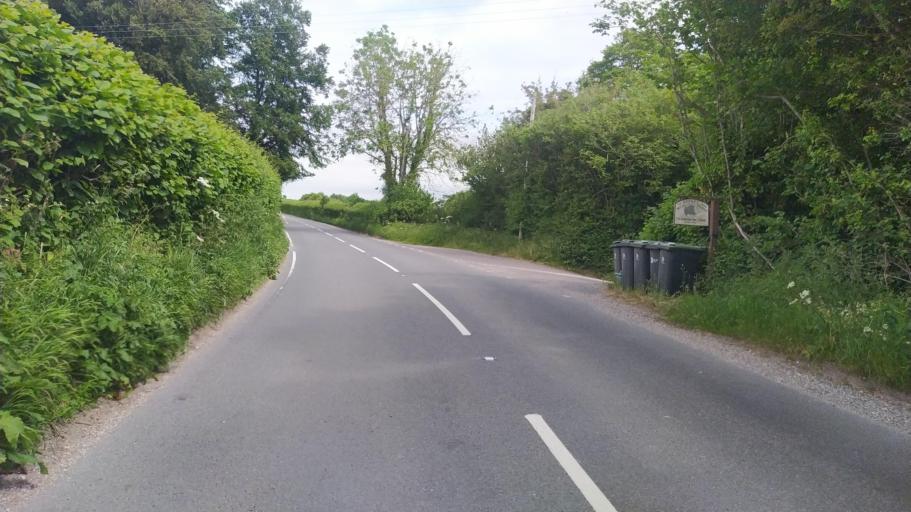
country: GB
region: England
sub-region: Dorset
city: Dorchester
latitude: 50.7879
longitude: -2.4729
